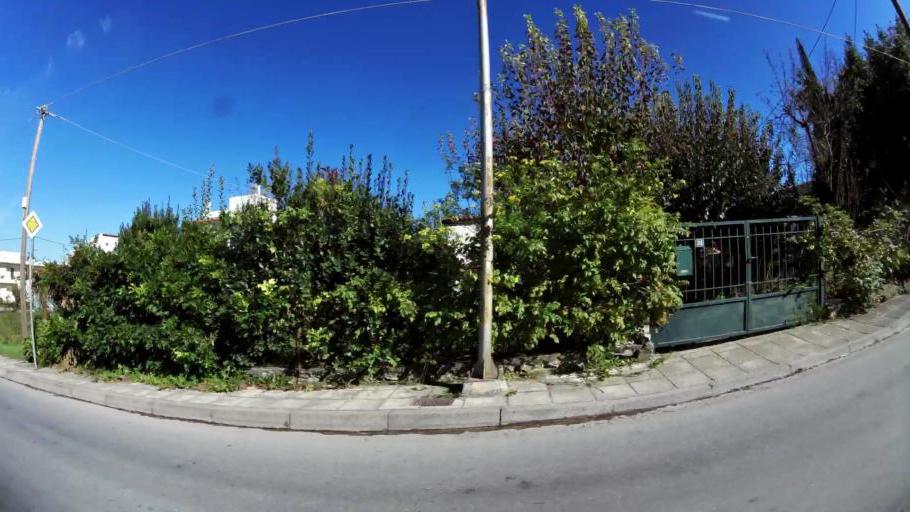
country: GR
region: Attica
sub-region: Nomarchia Anatolikis Attikis
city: Drosia
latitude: 38.1176
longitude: 23.8723
